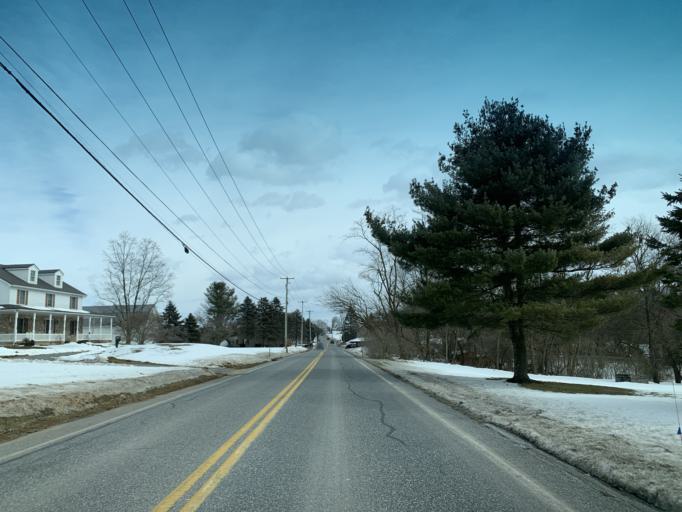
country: US
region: Pennsylvania
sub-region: York County
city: Shrewsbury
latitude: 39.7854
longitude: -76.6639
